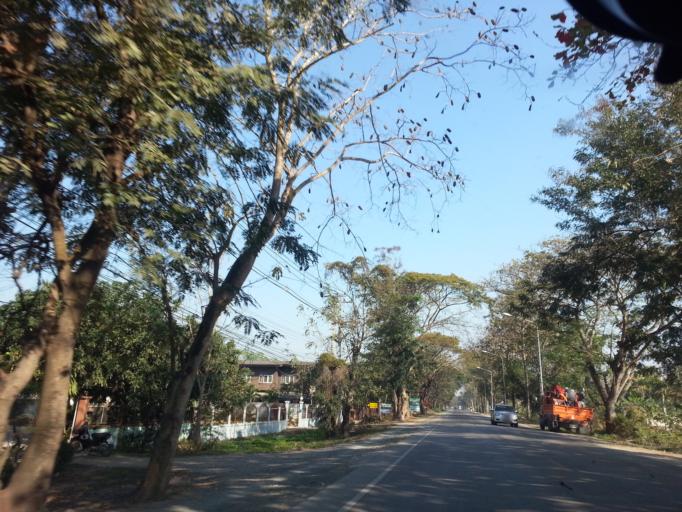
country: TH
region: Chiang Mai
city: San Sai
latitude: 18.9565
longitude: 98.9839
